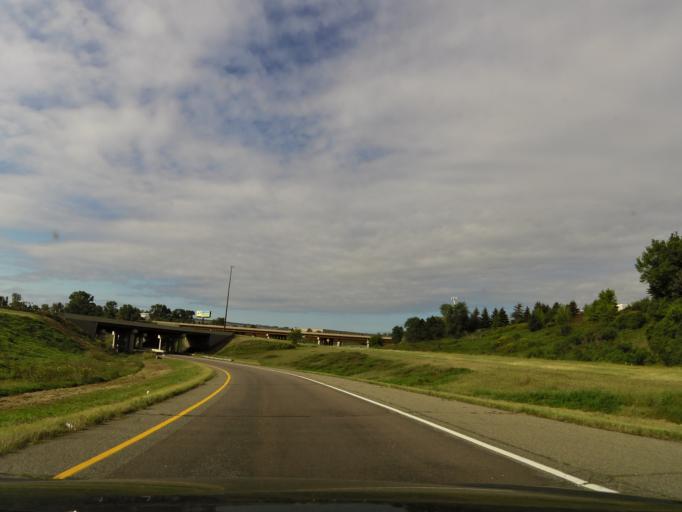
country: US
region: Minnesota
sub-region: Dakota County
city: Mendota Heights
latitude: 44.8641
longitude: -93.1471
